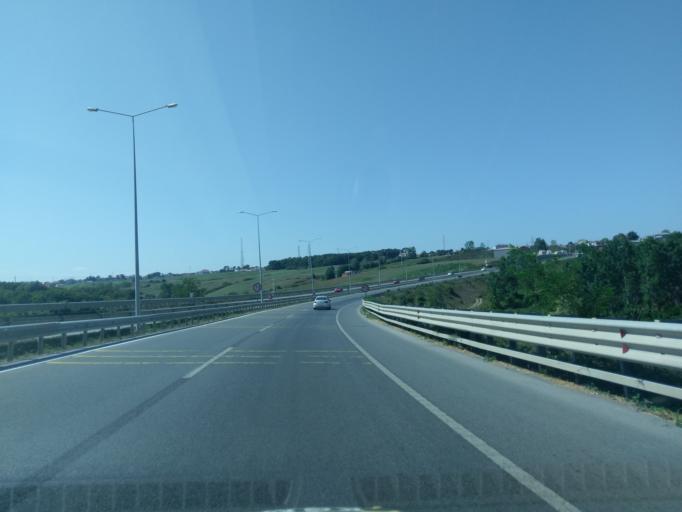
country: TR
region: Samsun
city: Bafra
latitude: 41.5413
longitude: 35.9335
